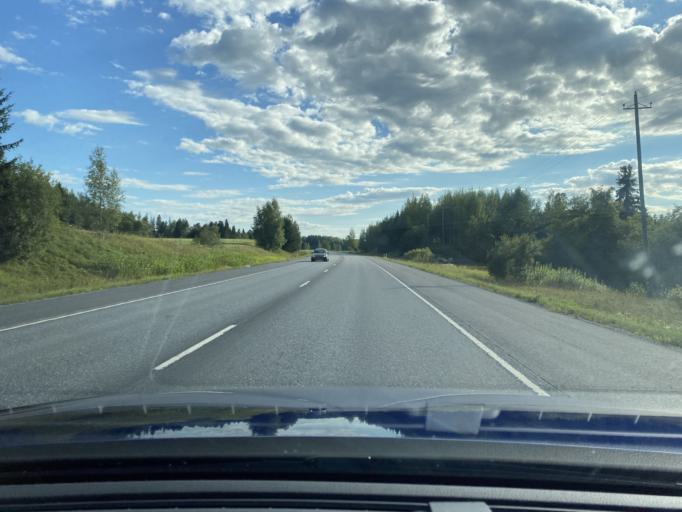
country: FI
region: Pirkanmaa
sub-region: Tampere
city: Lempaeaelae
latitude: 61.3347
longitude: 23.7802
